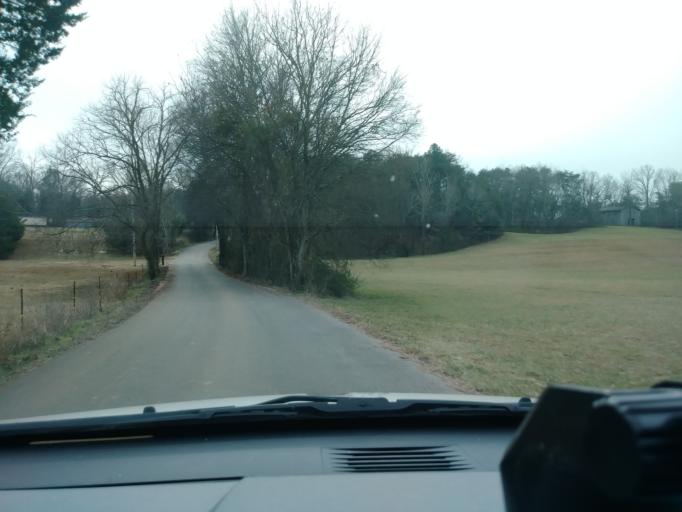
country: US
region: Tennessee
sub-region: Greene County
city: Greeneville
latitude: 36.0841
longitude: -82.8893
